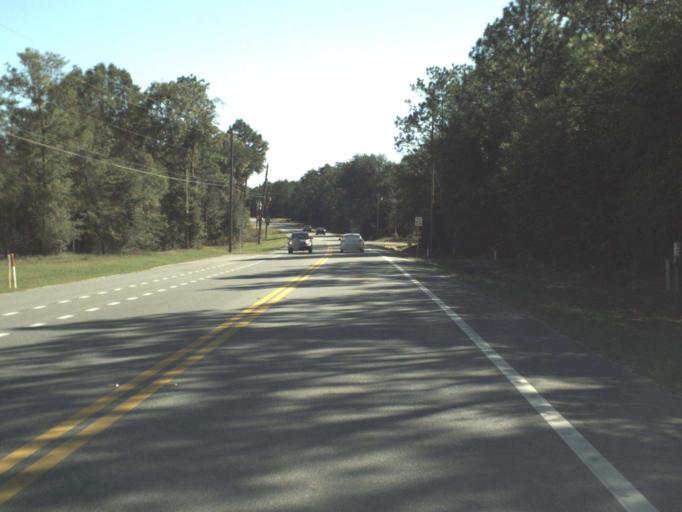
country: US
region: Florida
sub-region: Okaloosa County
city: Crestview
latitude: 30.7644
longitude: -86.6667
